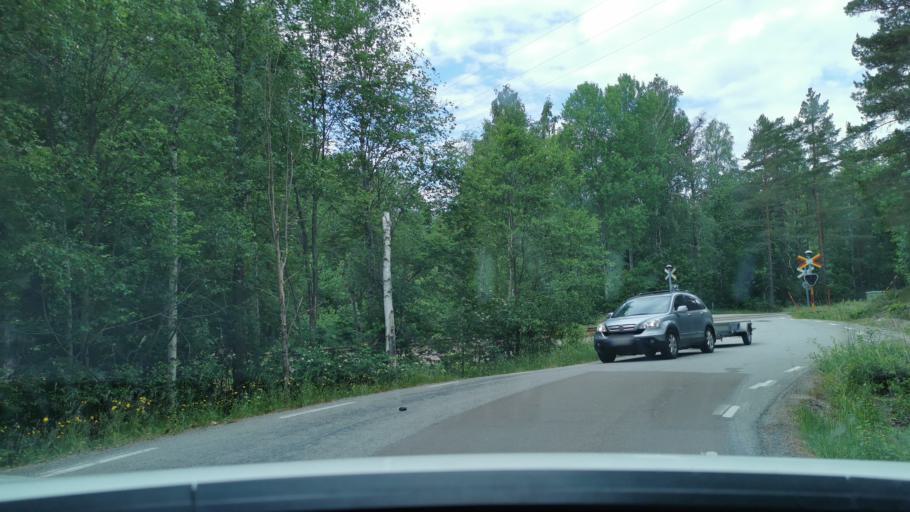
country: SE
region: Vaestra Goetaland
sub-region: Bengtsfors Kommun
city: Dals Langed
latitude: 58.8349
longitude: 12.4104
